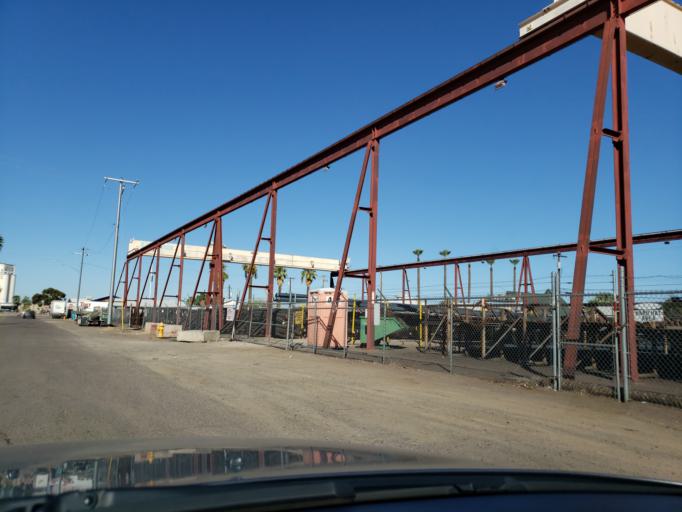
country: US
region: Arizona
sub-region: Maricopa County
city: Phoenix
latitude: 33.4450
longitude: -112.1055
